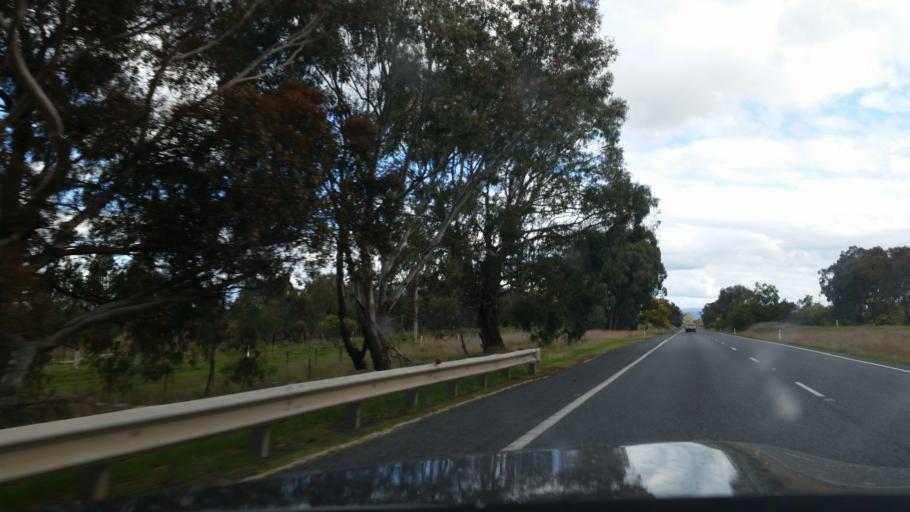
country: AU
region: New South Wales
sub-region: Albury Municipality
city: Lavington
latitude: -35.9840
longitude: 146.9989
